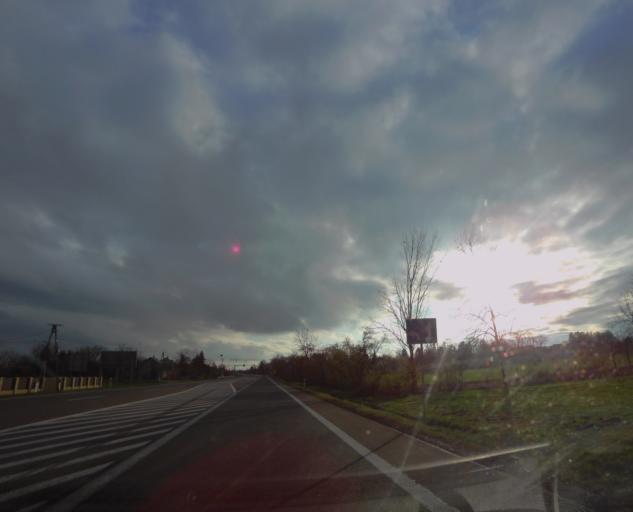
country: PL
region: Subcarpathian Voivodeship
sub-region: Powiat przemyski
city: Orly
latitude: 49.9024
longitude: 22.8170
